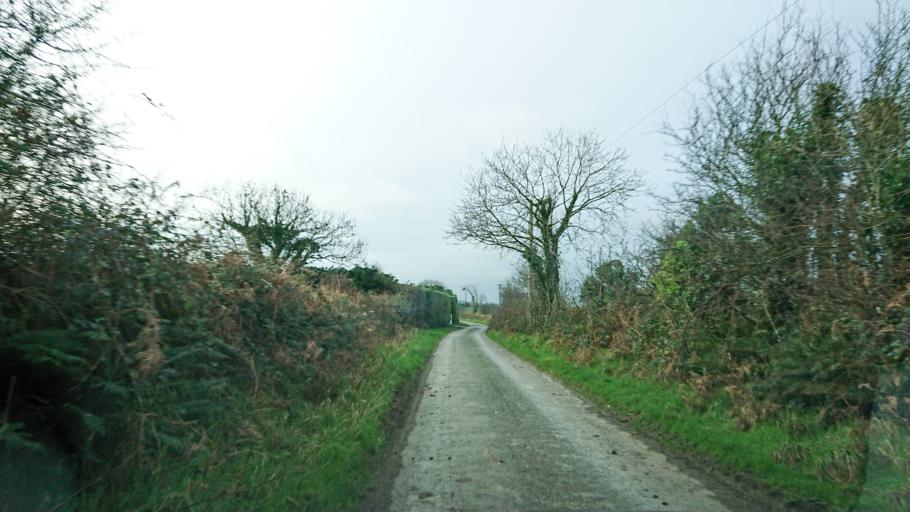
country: IE
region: Munster
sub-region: Waterford
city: Tra Mhor
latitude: 52.1953
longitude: -7.1710
